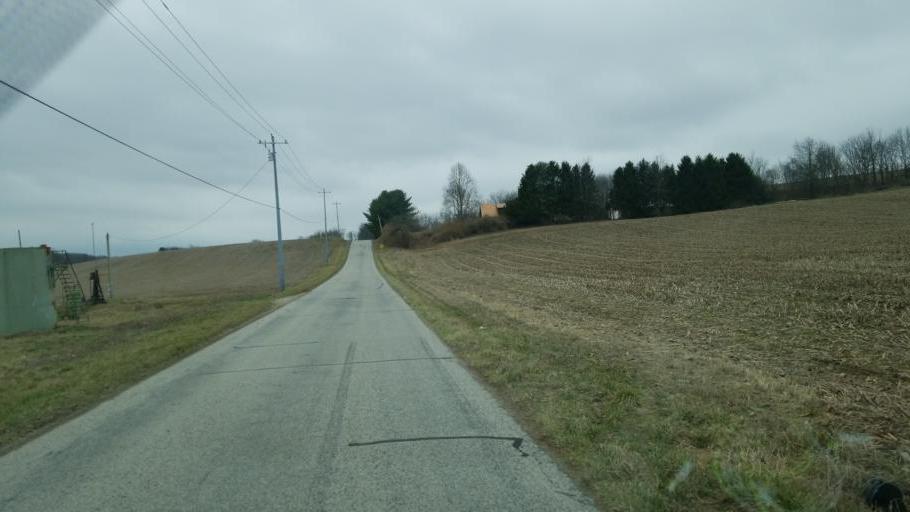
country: US
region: Ohio
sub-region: Licking County
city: Utica
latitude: 40.1967
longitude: -82.4012
